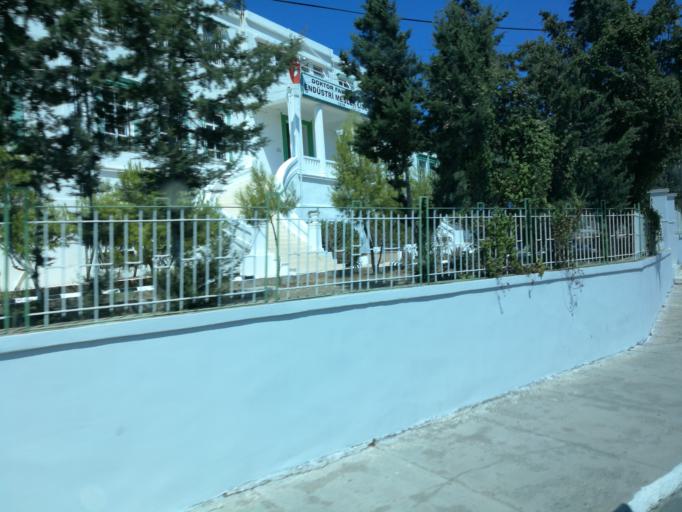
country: CY
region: Ammochostos
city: Famagusta
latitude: 35.1124
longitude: 33.9451
